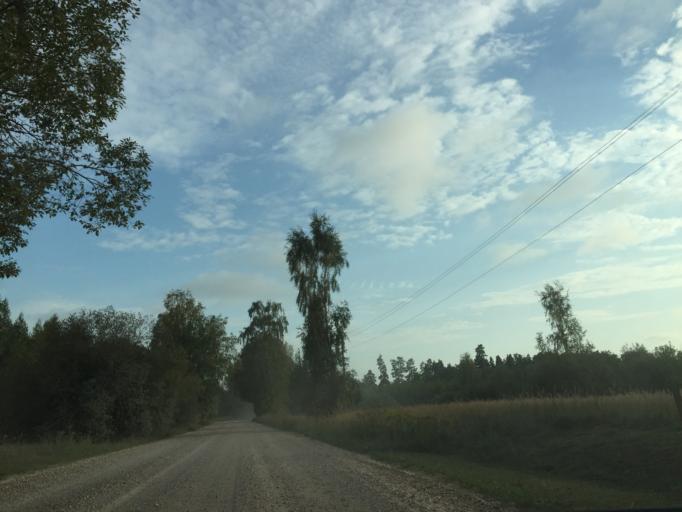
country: LV
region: Ikskile
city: Ikskile
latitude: 56.8182
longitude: 24.4487
